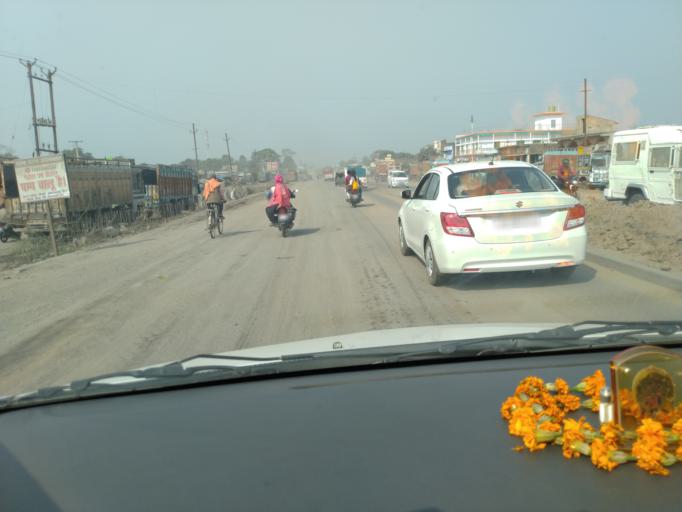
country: IN
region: Bihar
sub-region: Rohtas
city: Dehri
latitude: 24.9137
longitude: 84.1620
